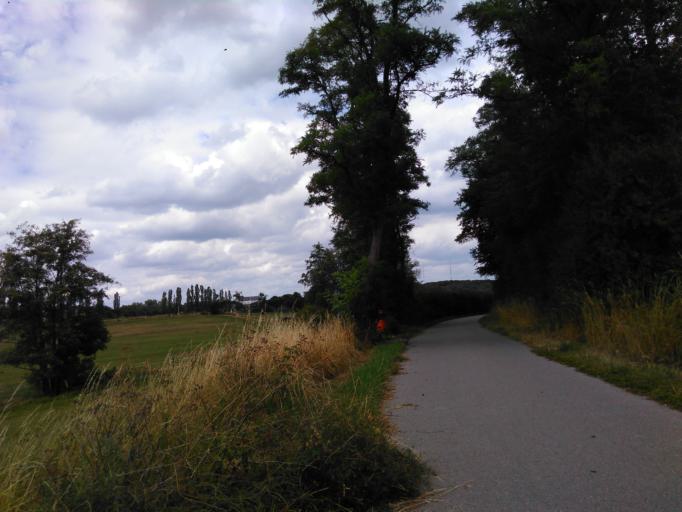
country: LU
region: Grevenmacher
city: Gonderange
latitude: 49.6884
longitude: 6.2494
